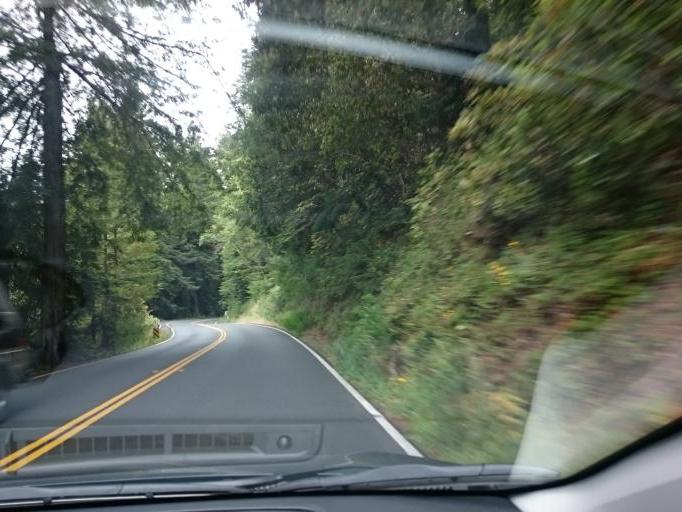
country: US
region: California
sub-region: Mendocino County
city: Fort Bragg
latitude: 39.1796
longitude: -123.7013
